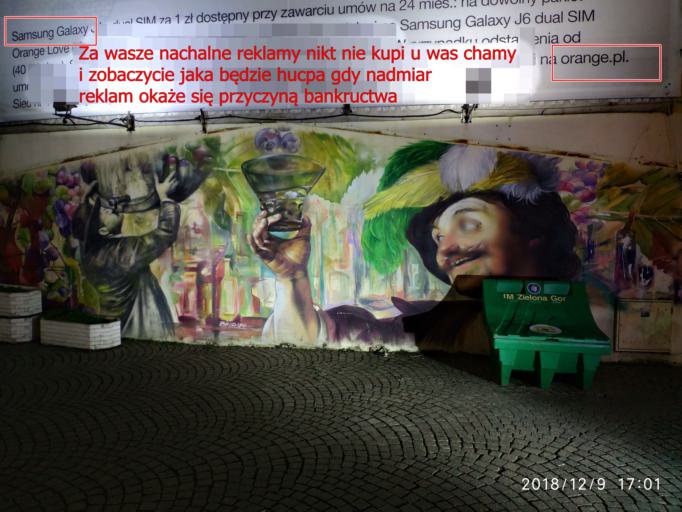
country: PL
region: Lubusz
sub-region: Zielona Gora
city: Zielona Gora
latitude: 51.9394
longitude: 15.5054
